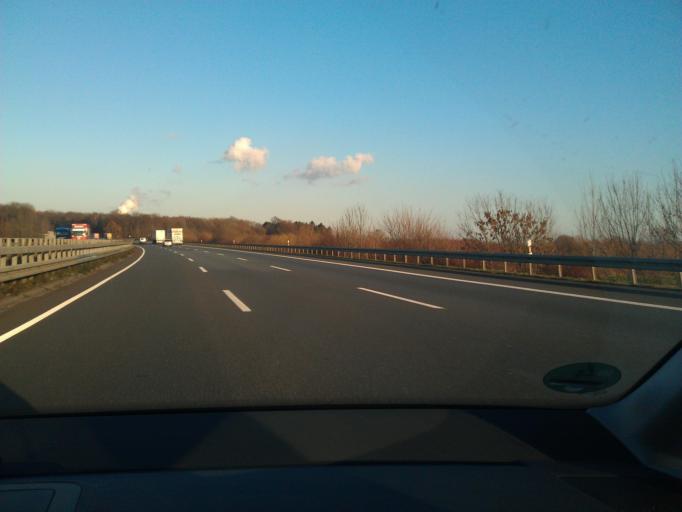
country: DE
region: North Rhine-Westphalia
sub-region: Regierungsbezirk Arnsberg
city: Welver
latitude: 51.6441
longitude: 7.9091
